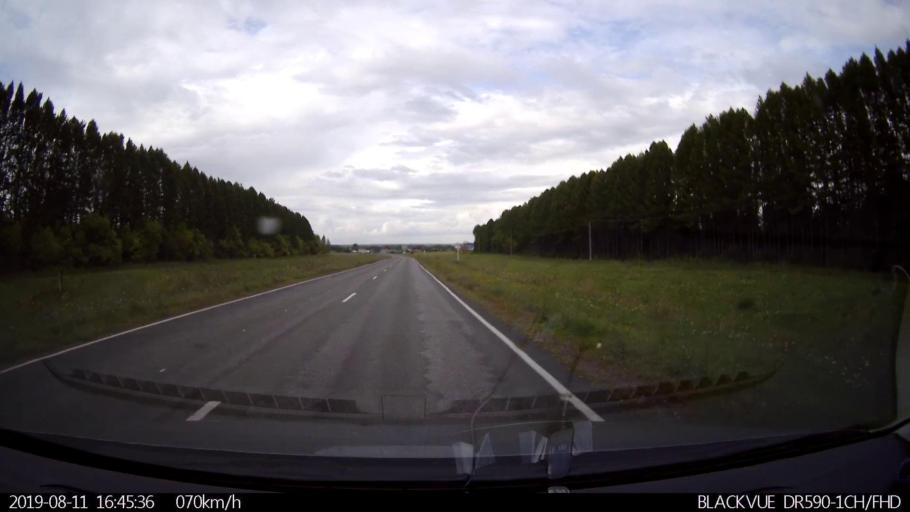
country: RU
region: Ulyanovsk
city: Mayna
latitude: 54.1915
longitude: 47.6871
